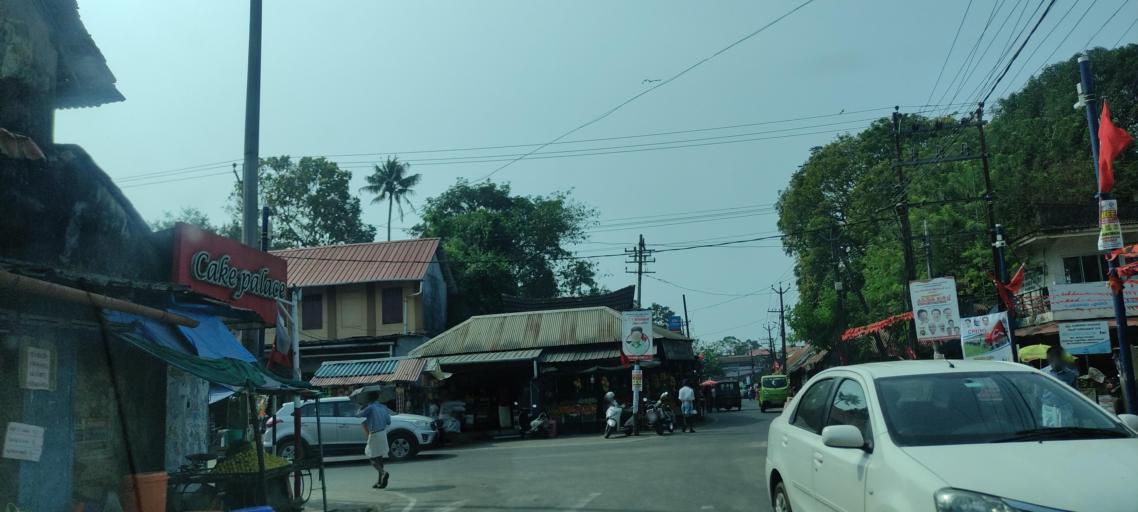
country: IN
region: Kerala
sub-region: Alappuzha
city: Vayalar
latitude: 9.6869
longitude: 76.3366
